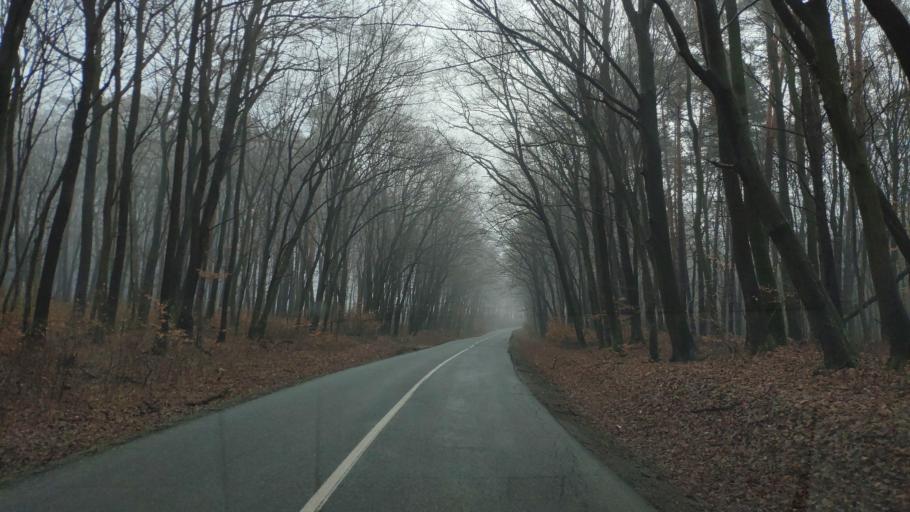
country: SK
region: Kosicky
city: Kosice
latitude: 48.7105
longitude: 21.3769
